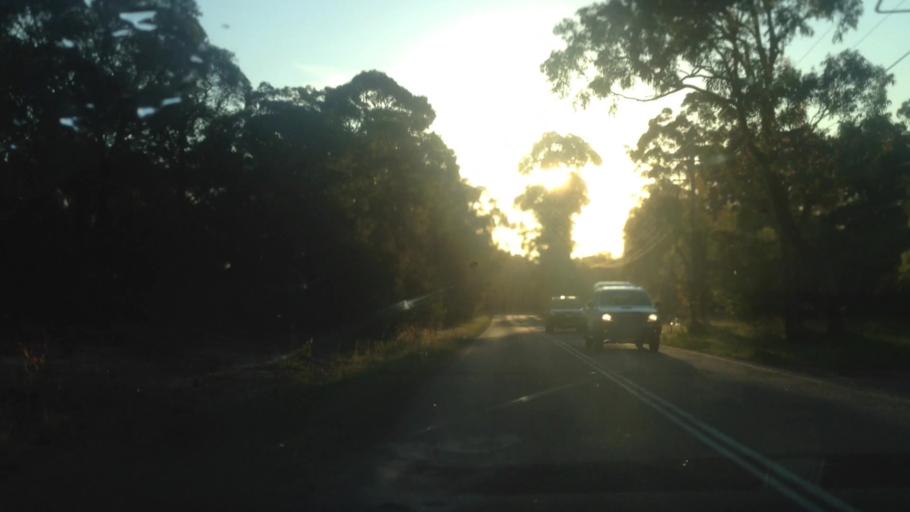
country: AU
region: New South Wales
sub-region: Wyong Shire
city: Kingfisher Shores
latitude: -33.1570
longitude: 151.5050
